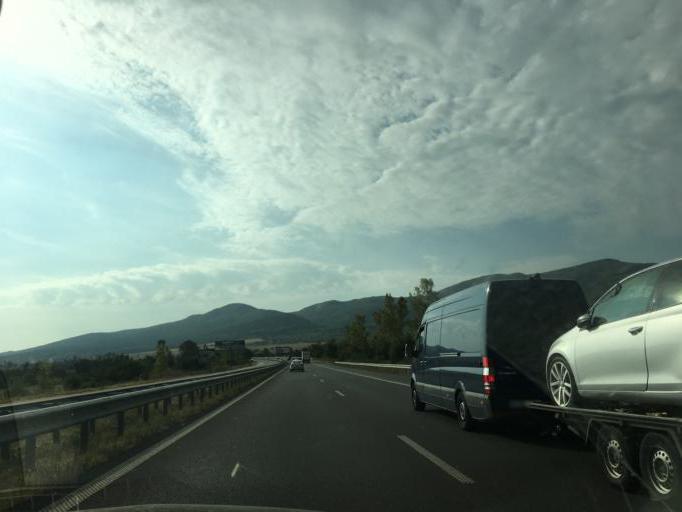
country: BG
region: Sofiya
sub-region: Obshtina Elin Pelin
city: Elin Pelin
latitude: 42.6200
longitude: 23.5226
